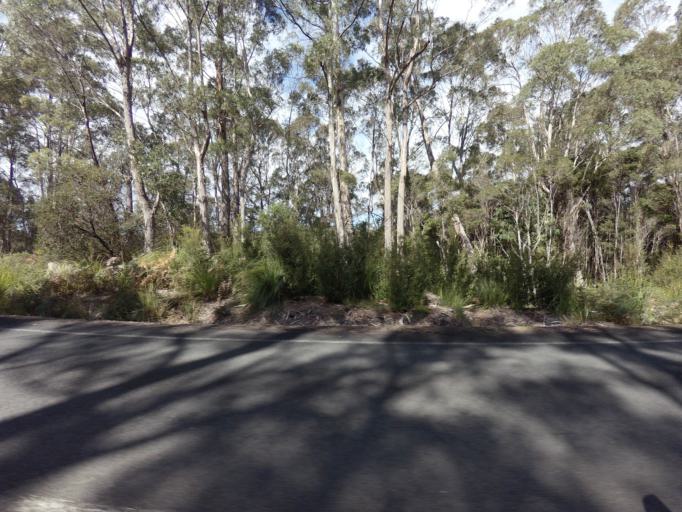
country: AU
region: Tasmania
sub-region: Huon Valley
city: Geeveston
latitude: -43.4132
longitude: 146.9403
